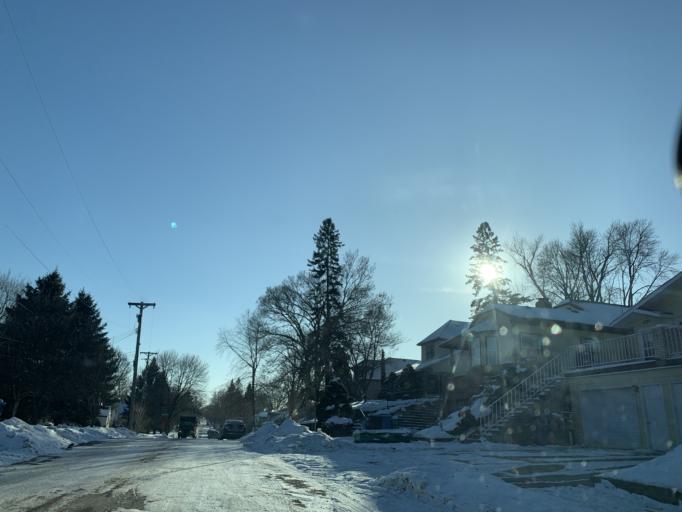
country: US
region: Minnesota
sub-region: Dakota County
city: Mendota Heights
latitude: 44.9097
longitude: -93.2076
